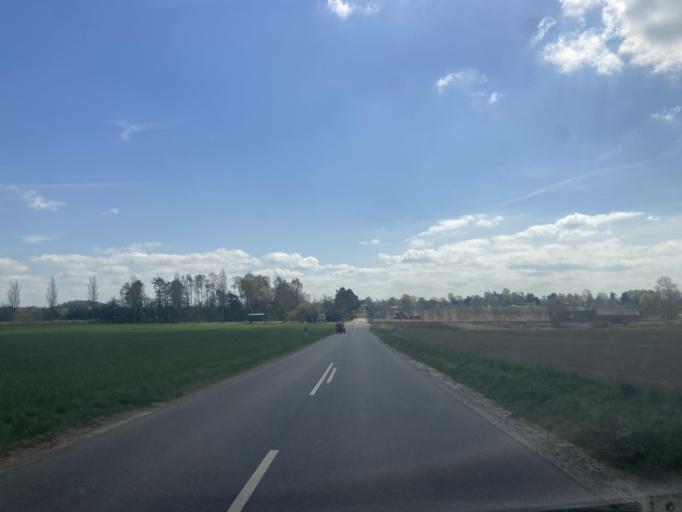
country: DK
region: Capital Region
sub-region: Gribskov Kommune
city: Helsinge
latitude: 56.0610
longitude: 12.1159
